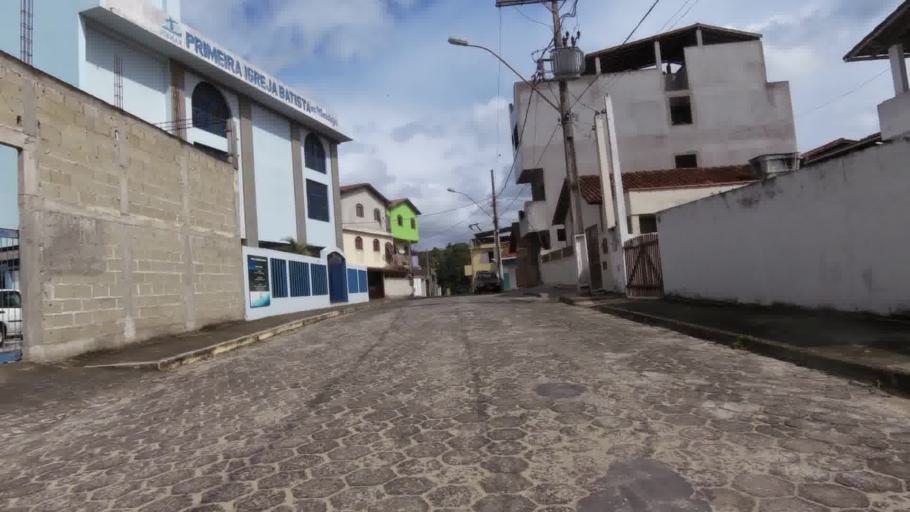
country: BR
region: Espirito Santo
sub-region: Marataizes
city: Marataizes
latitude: -21.0336
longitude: -40.8188
